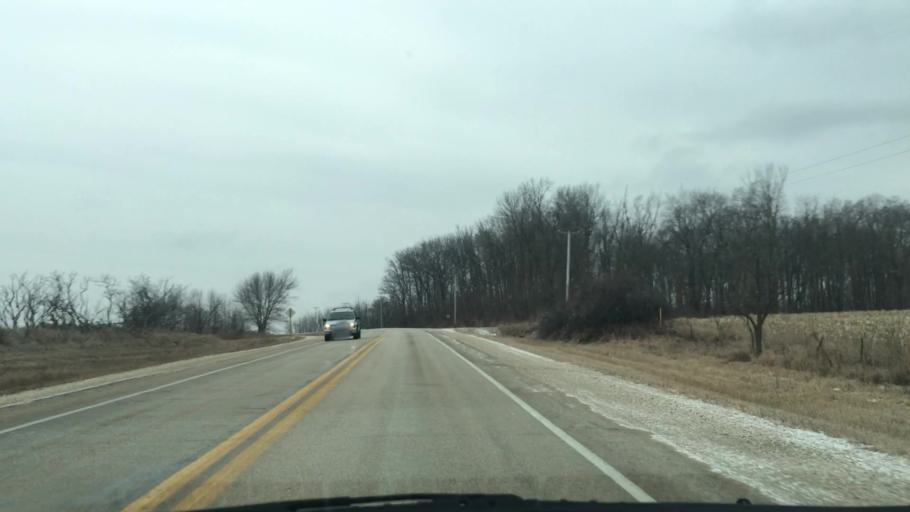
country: US
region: Iowa
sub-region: Fayette County
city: West Union
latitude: 43.0379
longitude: -91.8372
